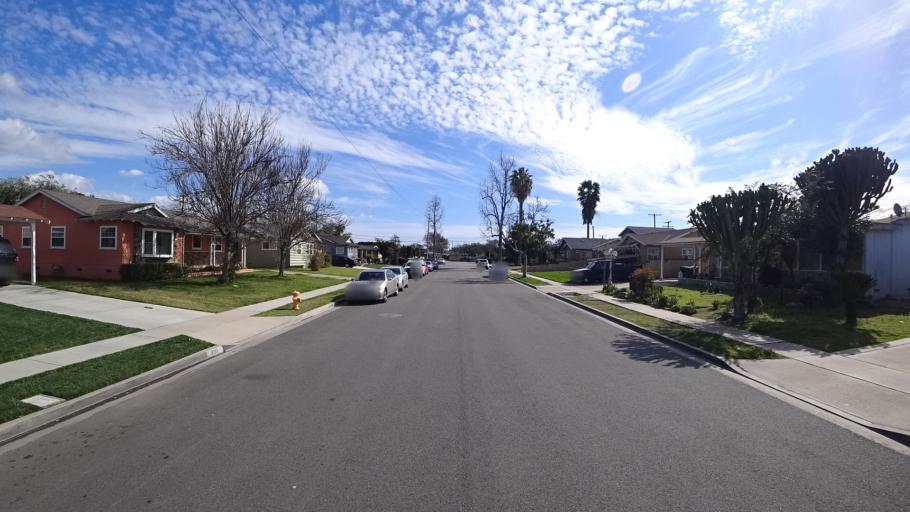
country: US
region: California
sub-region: Orange County
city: Anaheim
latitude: 33.8451
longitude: -117.9285
